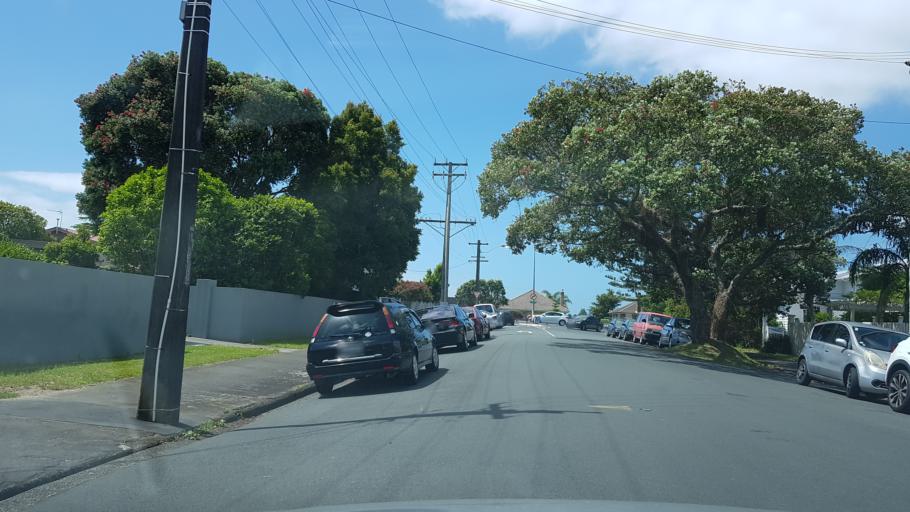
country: NZ
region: Auckland
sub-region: Auckland
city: North Shore
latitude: -36.8125
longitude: 174.7458
